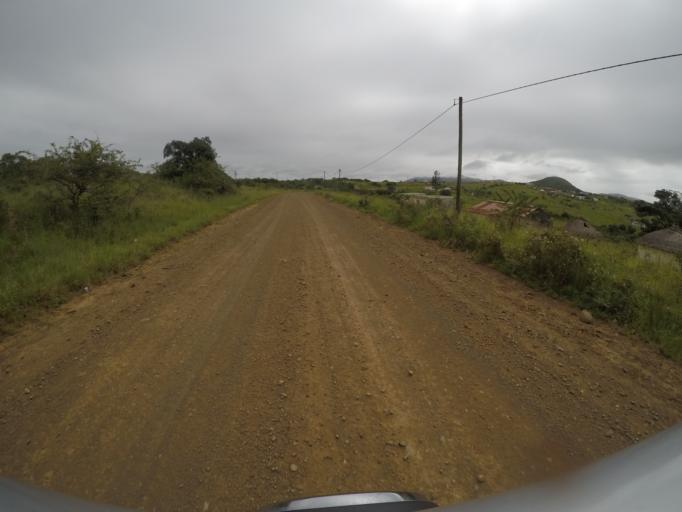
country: ZA
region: KwaZulu-Natal
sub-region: uThungulu District Municipality
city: Empangeni
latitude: -28.6046
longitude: 31.8380
